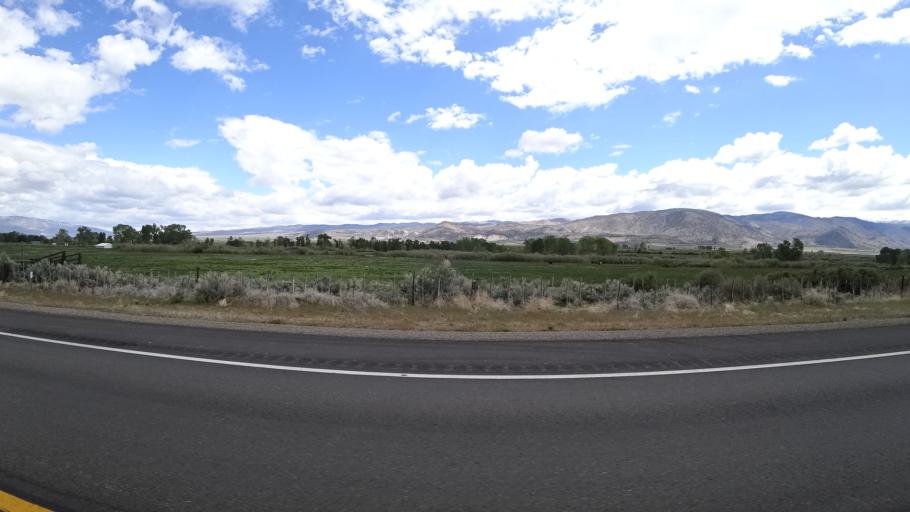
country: US
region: Nevada
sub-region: Lyon County
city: Smith Valley
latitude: 38.5737
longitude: -119.5107
